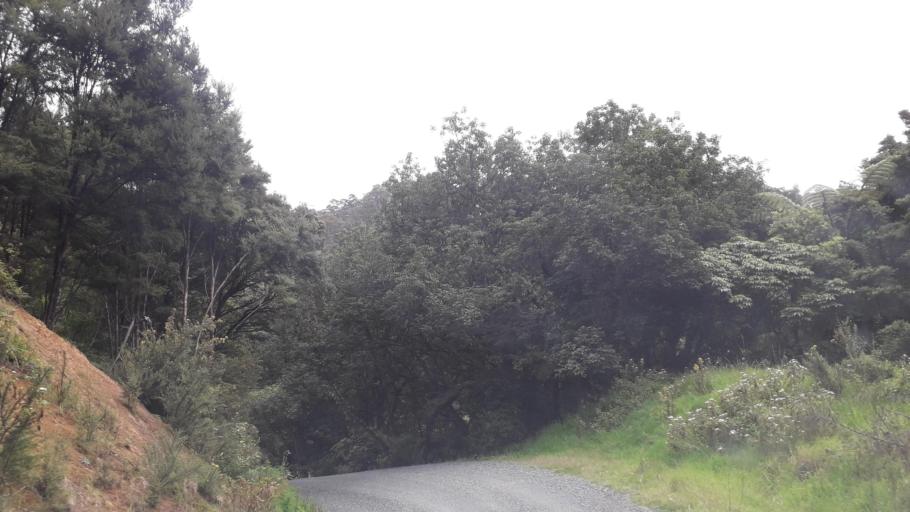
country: NZ
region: Northland
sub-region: Far North District
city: Taipa
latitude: -35.0850
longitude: 173.5506
